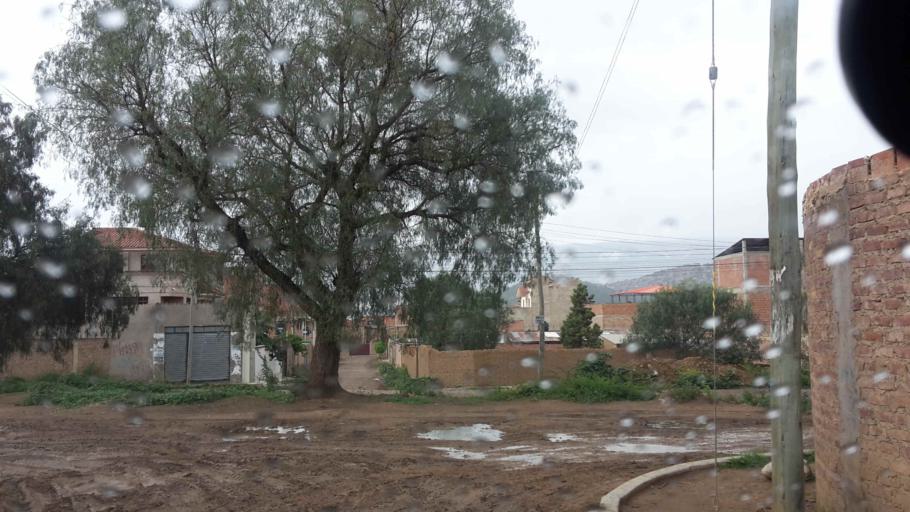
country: BO
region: Cochabamba
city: Cochabamba
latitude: -17.4472
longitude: -66.1567
